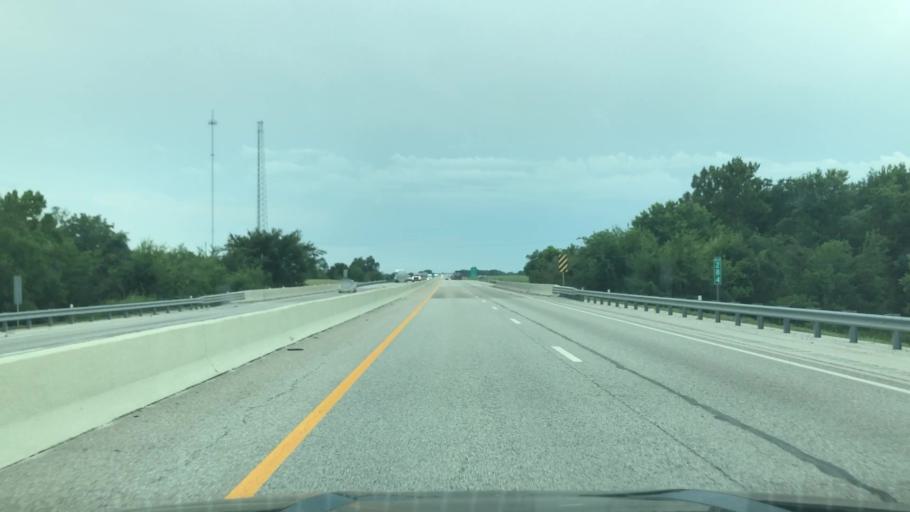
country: US
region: Oklahoma
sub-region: Craig County
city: Vinita
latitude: 36.5842
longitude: -95.2019
